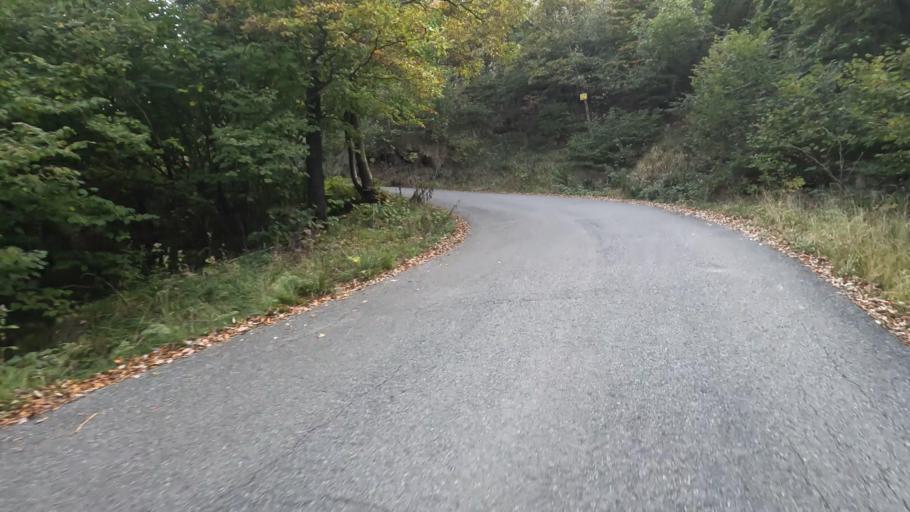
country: IT
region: Liguria
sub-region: Provincia di Genova
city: Sciarborasca
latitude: 44.4373
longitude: 8.5849
